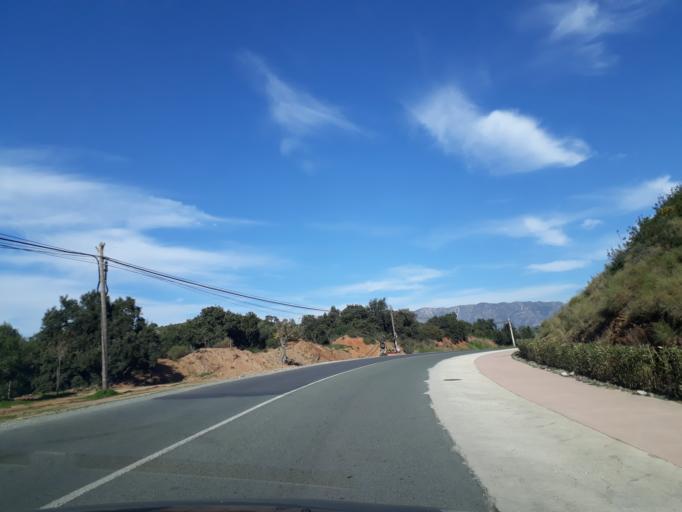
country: ES
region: Andalusia
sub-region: Provincia de Malaga
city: Fuengirola
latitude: 36.5116
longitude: -4.6878
